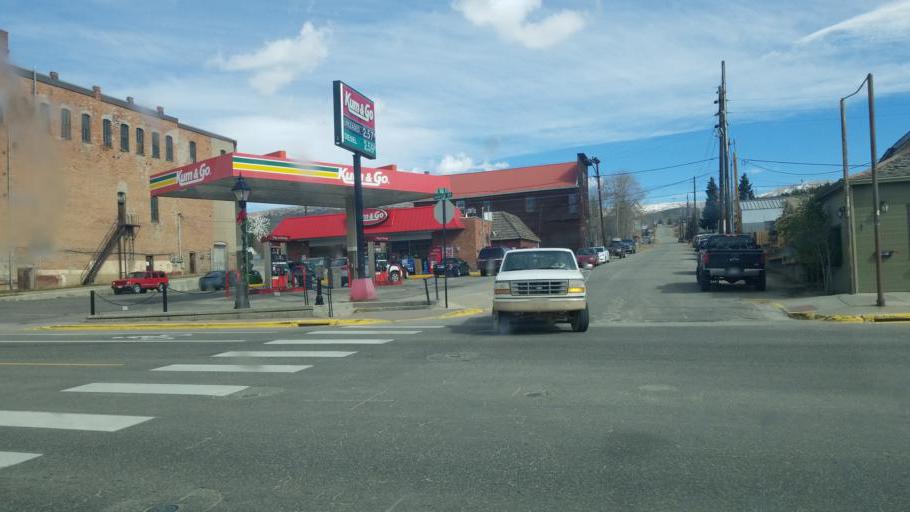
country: US
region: Colorado
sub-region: Lake County
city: Leadville
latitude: 39.2462
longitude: -106.2910
